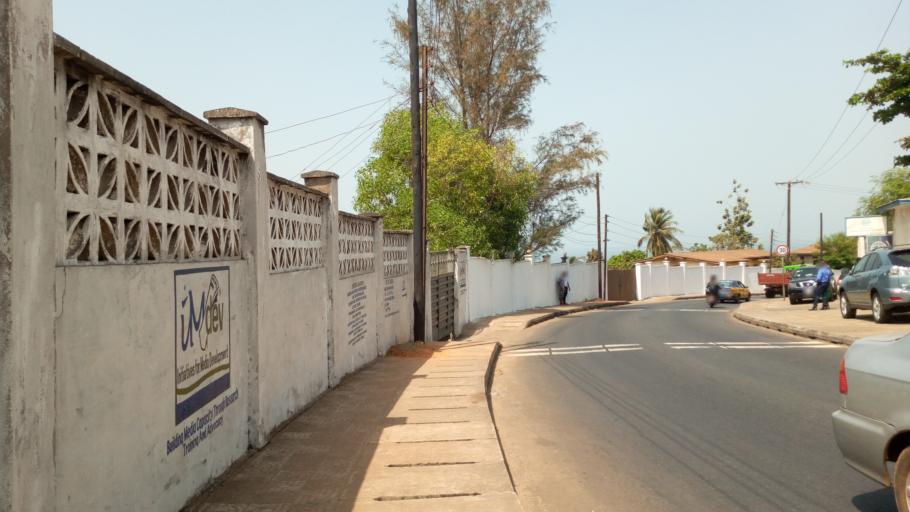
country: SL
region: Western Area
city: Freetown
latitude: 8.4824
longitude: -13.2634
